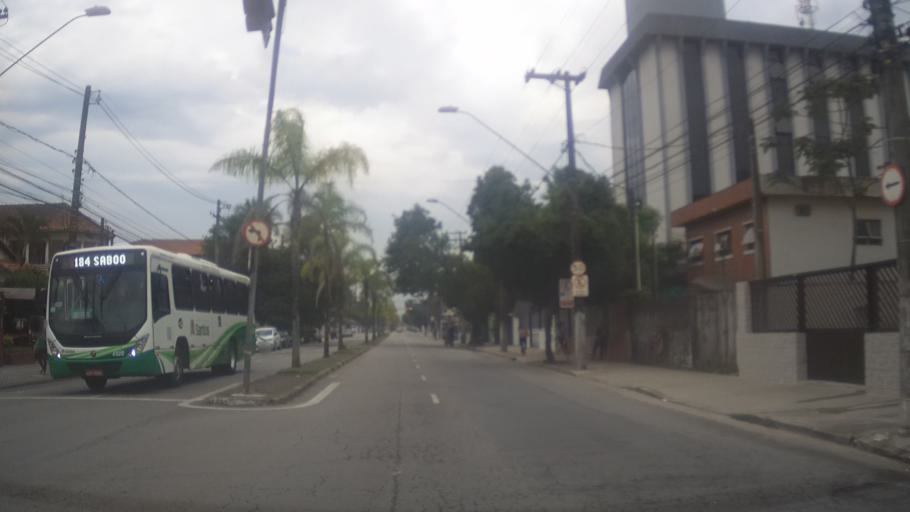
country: BR
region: Sao Paulo
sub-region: Santos
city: Santos
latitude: -23.9451
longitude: -46.3216
